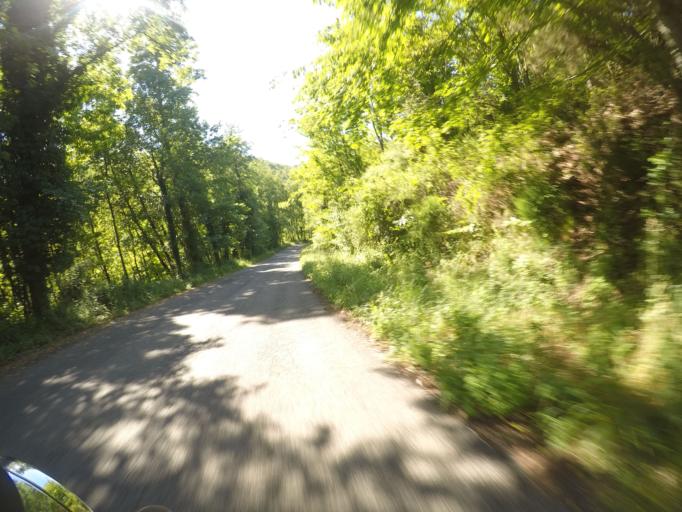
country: IT
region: Tuscany
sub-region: Provincia di Massa-Carrara
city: Fosdinovo
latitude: 44.1439
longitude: 10.0861
